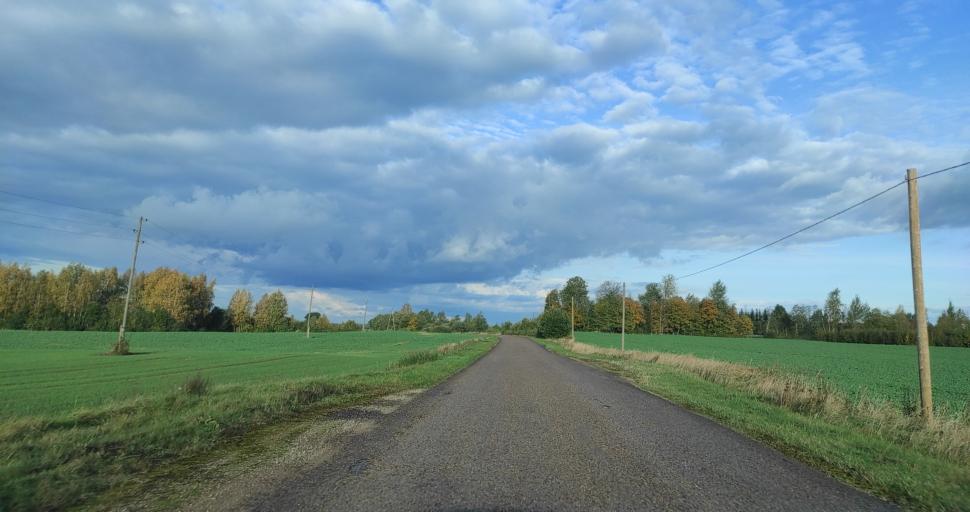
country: LV
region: Aizpute
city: Aizpute
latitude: 56.7786
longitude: 21.7767
